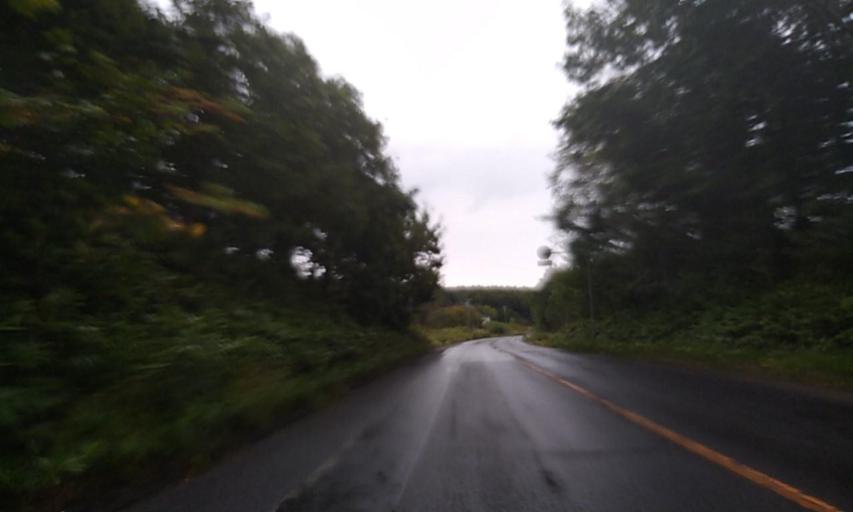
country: JP
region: Hokkaido
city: Mombetsu
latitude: 44.4822
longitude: 143.1019
